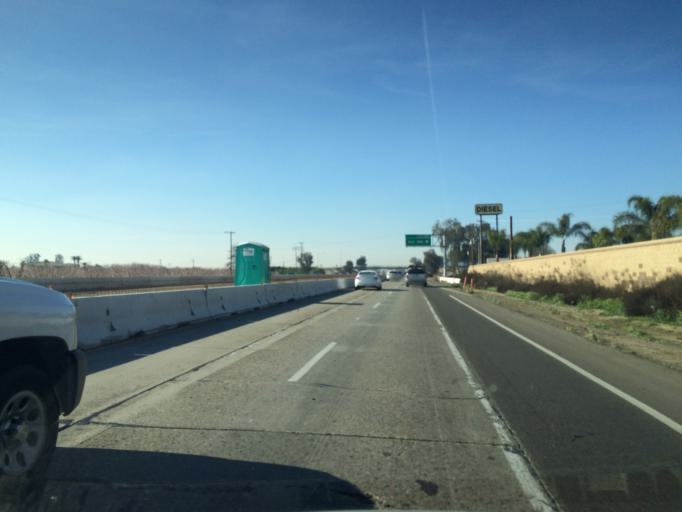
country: US
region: California
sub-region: Fresno County
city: Kingsburg
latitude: 36.4879
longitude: -119.5146
